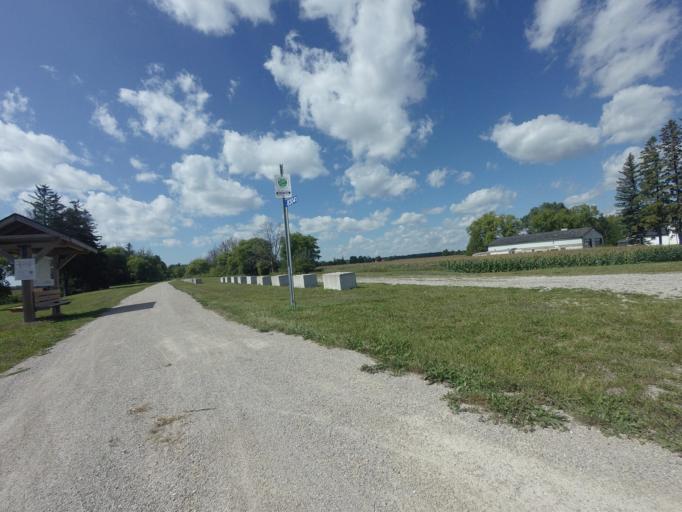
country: CA
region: Ontario
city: Huron East
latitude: 43.6804
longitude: -81.2999
